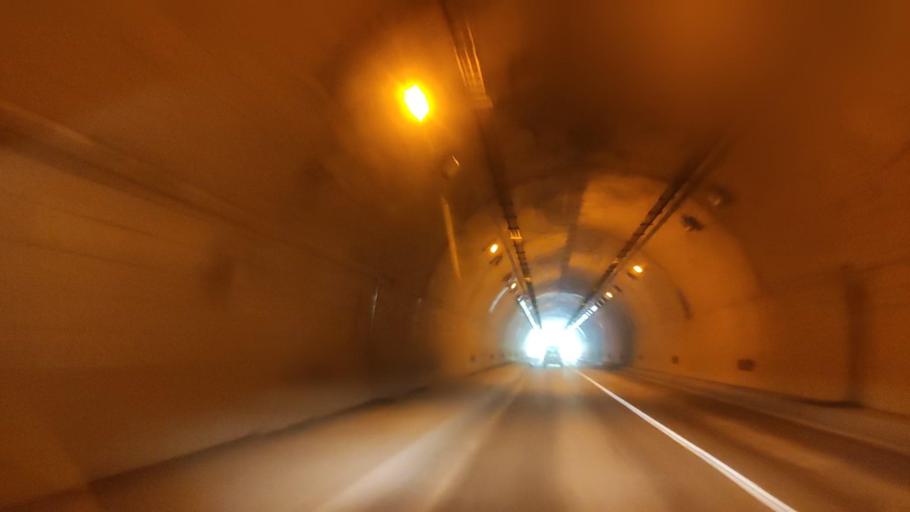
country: JP
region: Hokkaido
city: Bibai
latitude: 43.2402
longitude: 142.0280
